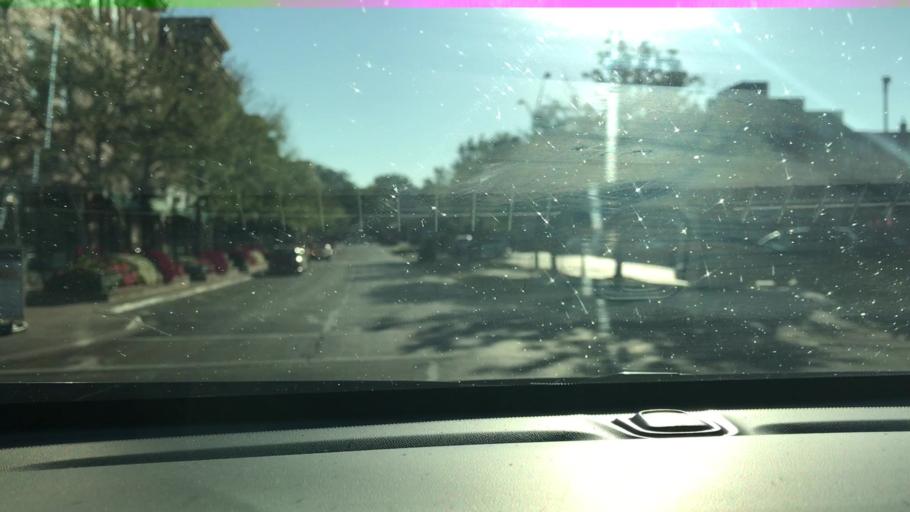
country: US
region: Illinois
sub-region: DuPage County
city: Naperville
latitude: 41.7741
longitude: -88.1512
